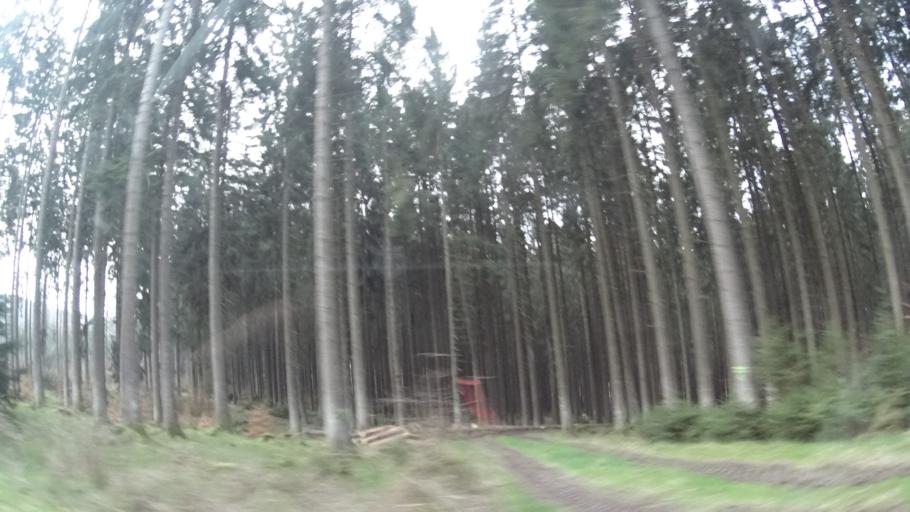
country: DE
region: Rheinland-Pfalz
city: Hattgenstein
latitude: 49.7213
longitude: 7.1518
